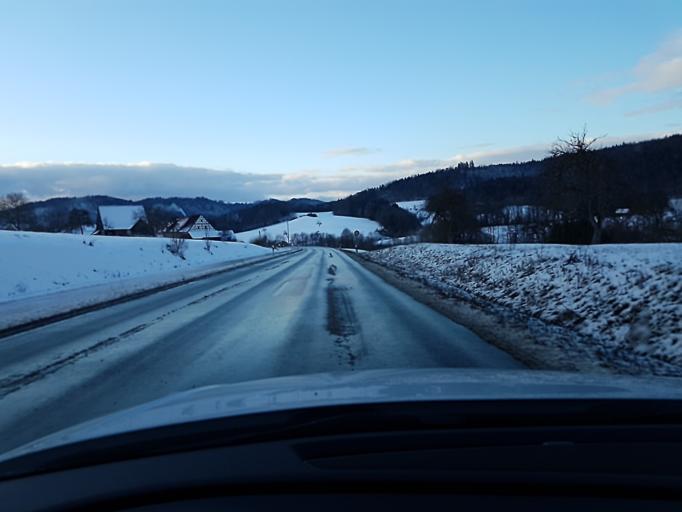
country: DE
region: Baden-Wuerttemberg
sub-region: Regierungsbezirk Stuttgart
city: Fichtenberg
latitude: 48.9810
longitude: 9.6775
